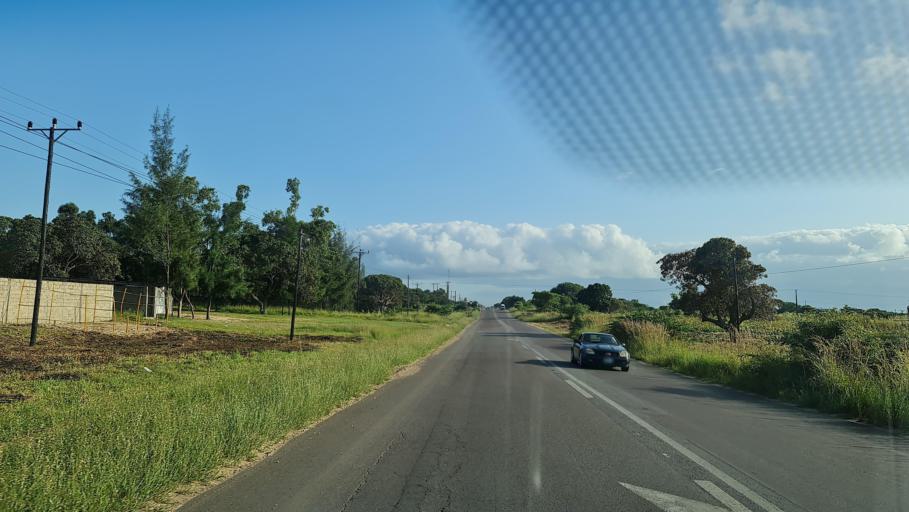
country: MZ
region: Maputo City
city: Maputo
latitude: -25.6784
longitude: 32.6670
